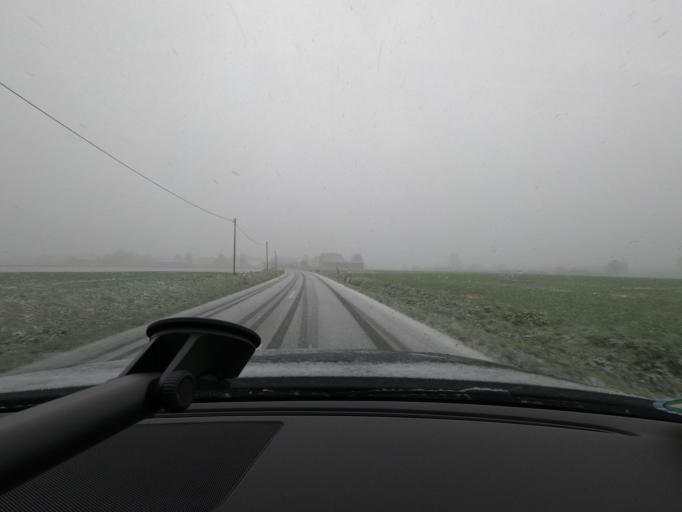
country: DE
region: North Rhine-Westphalia
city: Marsberg
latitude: 51.5189
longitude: 8.8569
